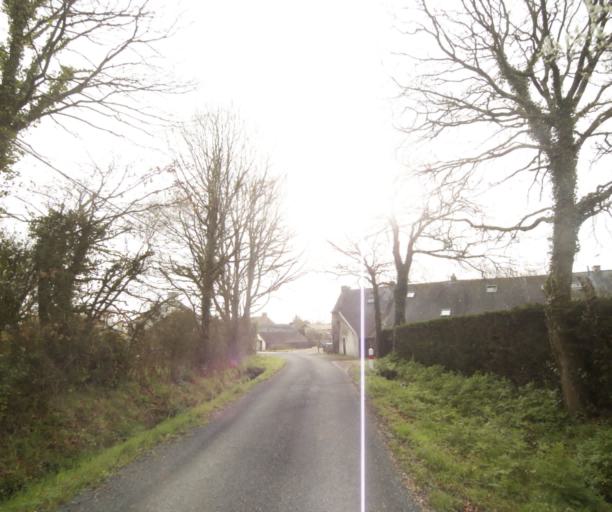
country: FR
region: Pays de la Loire
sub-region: Departement de la Loire-Atlantique
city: Bouvron
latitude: 47.4013
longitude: -1.8818
